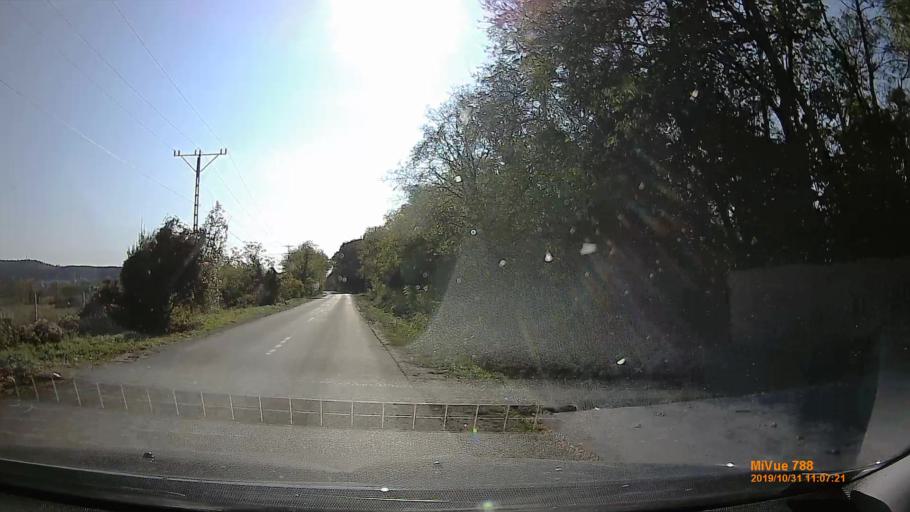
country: HU
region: Pest
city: Pilisborosjeno
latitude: 47.5973
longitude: 18.9989
